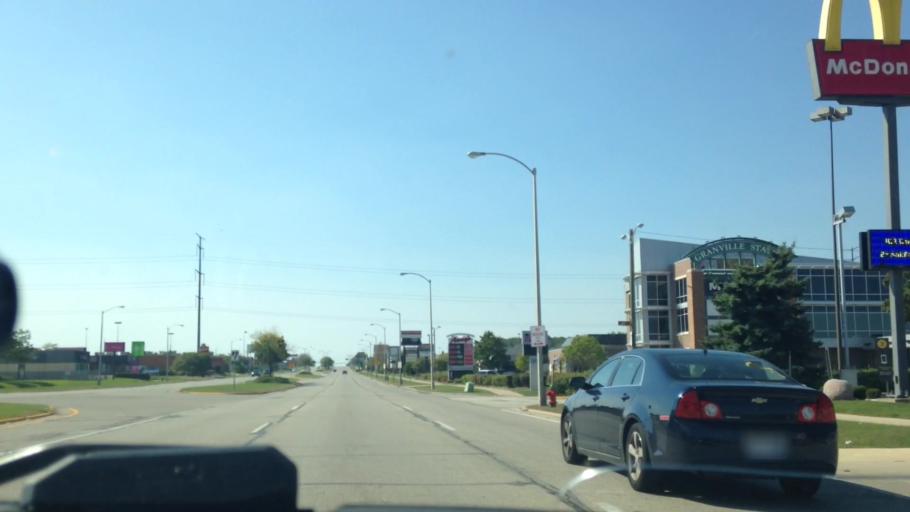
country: US
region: Wisconsin
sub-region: Milwaukee County
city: Brown Deer
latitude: 43.1779
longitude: -88.0109
